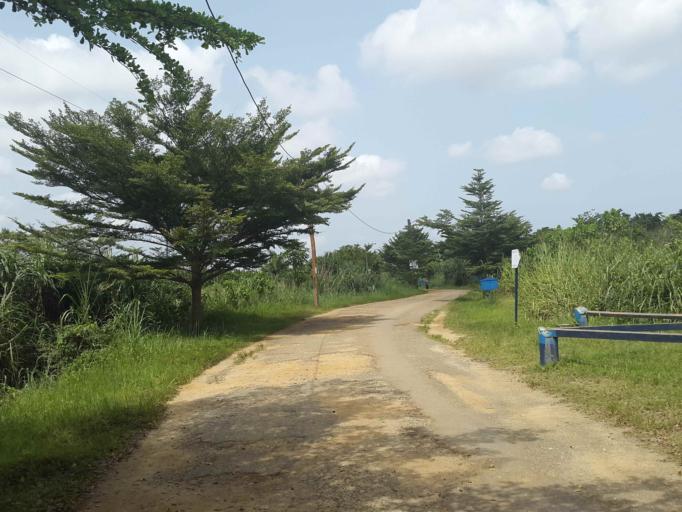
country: CM
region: Littoral
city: Douala
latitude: 4.0822
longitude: 9.7436
